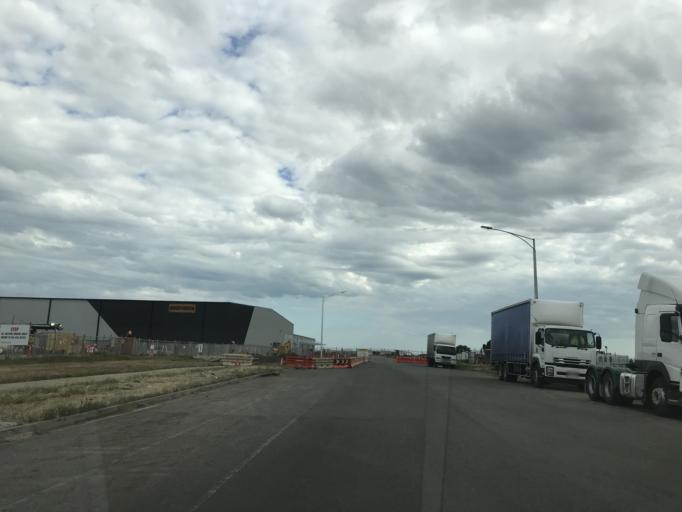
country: AU
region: Victoria
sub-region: Wyndham
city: Truganina
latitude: -37.8261
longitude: 144.7373
